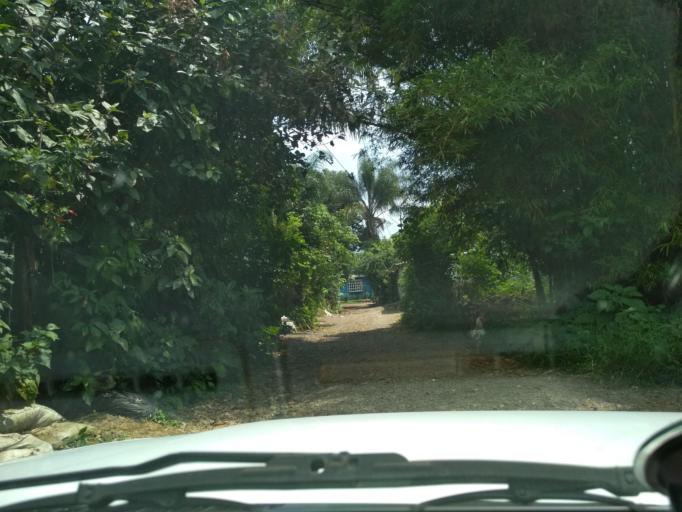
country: MX
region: Veracruz
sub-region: Ixtaczoquitlan
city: Buenavista
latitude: 18.8837
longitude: -97.0483
